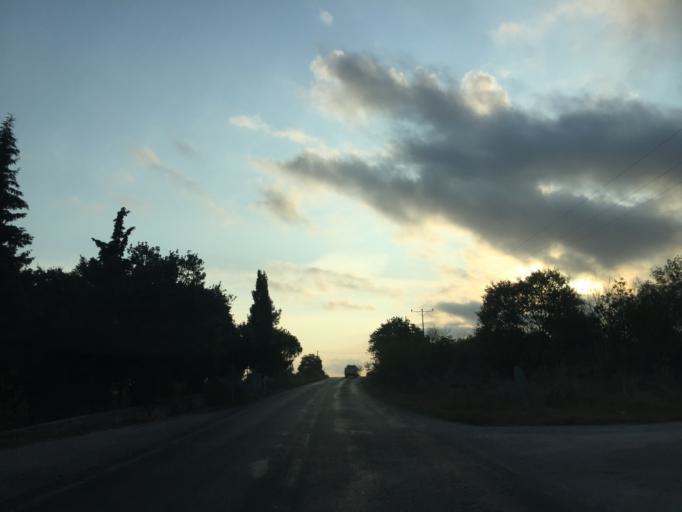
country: TR
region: Balikesir
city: Tutuncu
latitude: 40.1096
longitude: 27.7303
